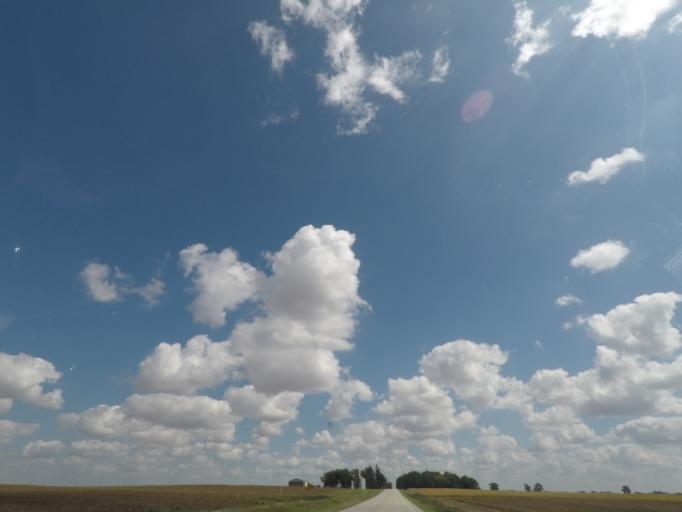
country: US
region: Iowa
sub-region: Story County
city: Nevada
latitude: 42.0779
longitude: -93.3828
